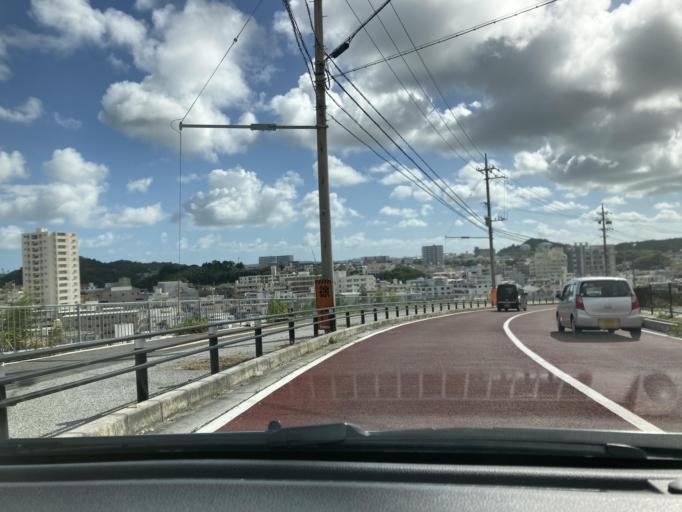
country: JP
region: Okinawa
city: Tomigusuku
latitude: 26.1995
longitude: 127.7297
